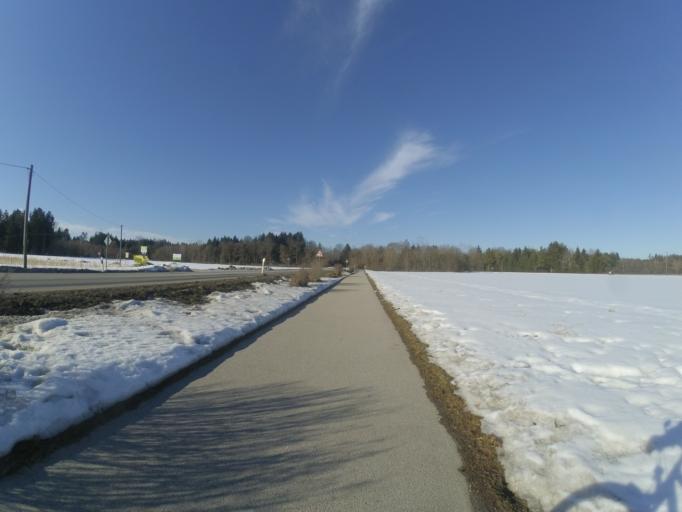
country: DE
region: Bavaria
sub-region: Upper Bavaria
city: Hohenkirchen-Siegertsbrunn
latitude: 47.9970
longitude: 11.7331
